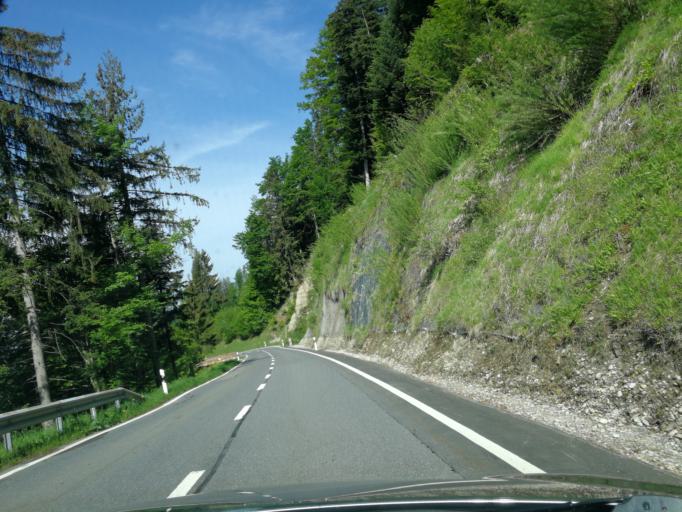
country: CH
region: Bern
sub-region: Emmental District
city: Eggiwil
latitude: 46.8245
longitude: 7.7911
